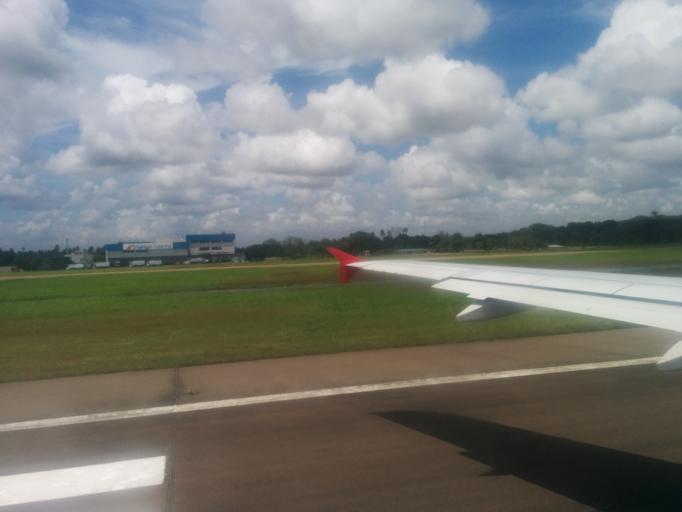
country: LK
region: Western
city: Katunayaka
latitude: 7.1919
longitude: 79.8921
